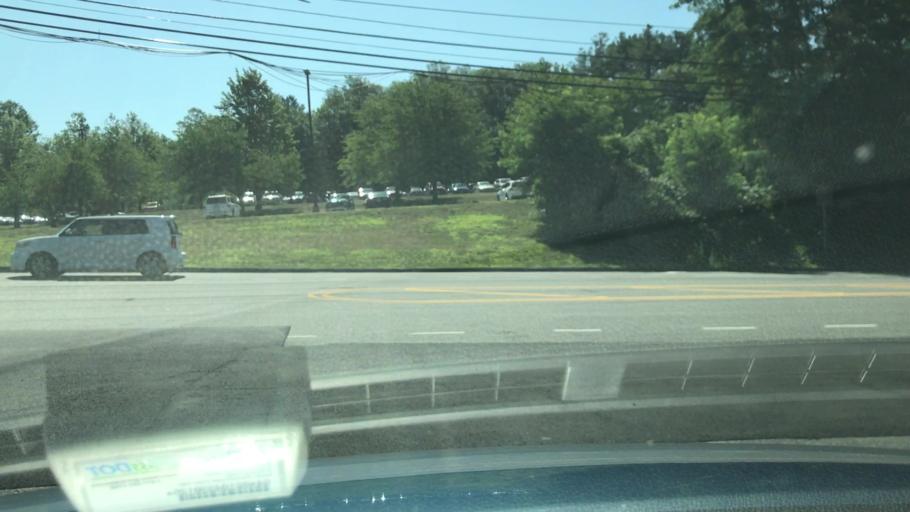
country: US
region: Massachusetts
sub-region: Middlesex County
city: Marlborough
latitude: 42.3234
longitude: -71.5789
